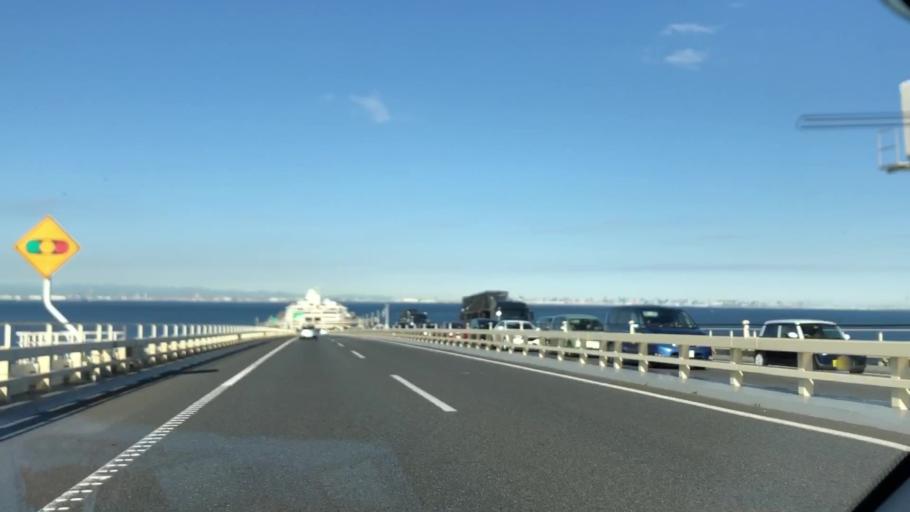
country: JP
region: Chiba
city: Kisarazu
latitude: 35.4578
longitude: 139.8836
